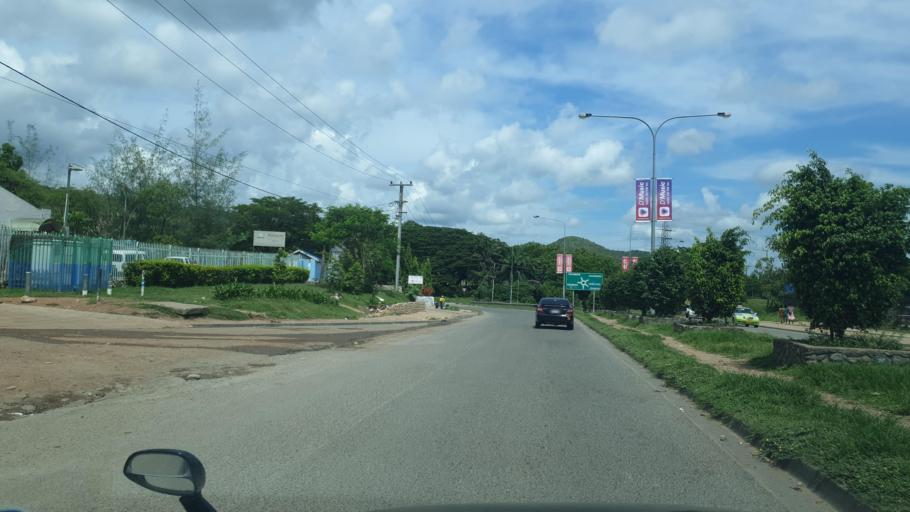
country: PG
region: National Capital
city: Port Moresby
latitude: -9.3992
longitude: 147.1603
